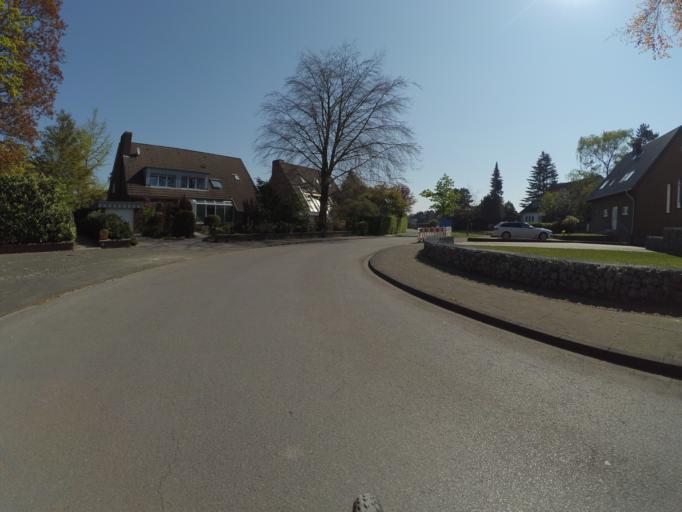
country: DE
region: North Rhine-Westphalia
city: Ludinghausen
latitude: 51.7710
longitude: 7.4330
